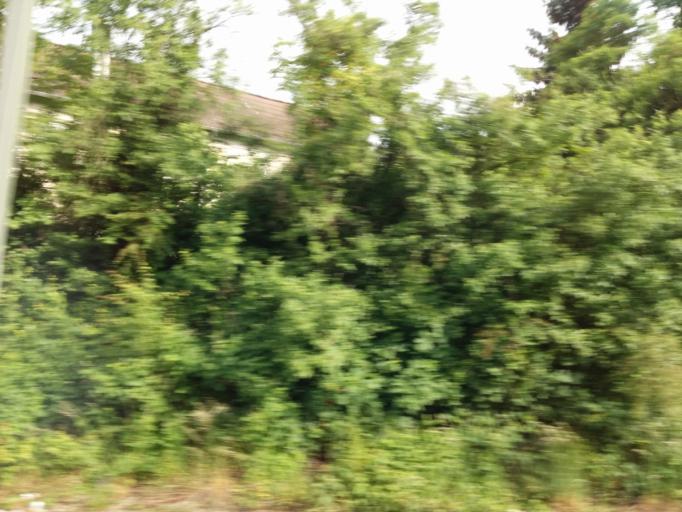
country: DE
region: Baden-Wuerttemberg
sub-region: Regierungsbezirk Stuttgart
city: Schwaigern
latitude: 49.1391
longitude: 9.0630
